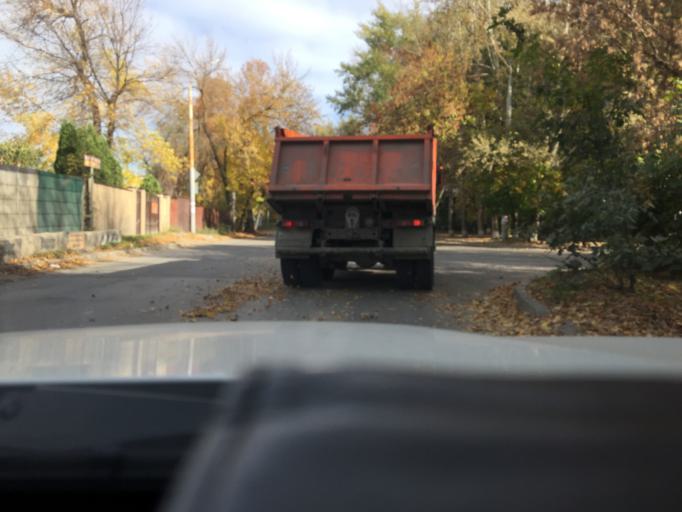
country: RU
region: Rostov
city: Imeni Chkalova
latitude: 47.2820
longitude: 39.8001
